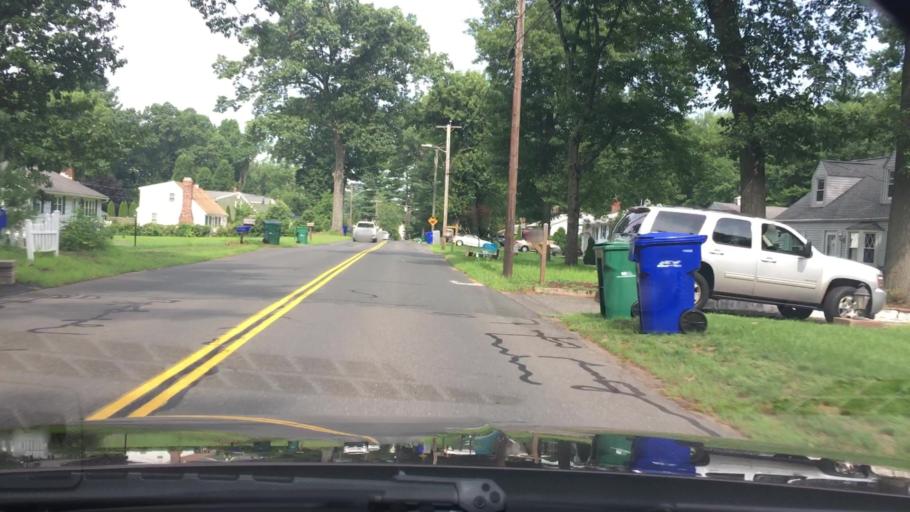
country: US
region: Connecticut
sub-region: Hartford County
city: South Windsor
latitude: 41.8257
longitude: -72.5856
